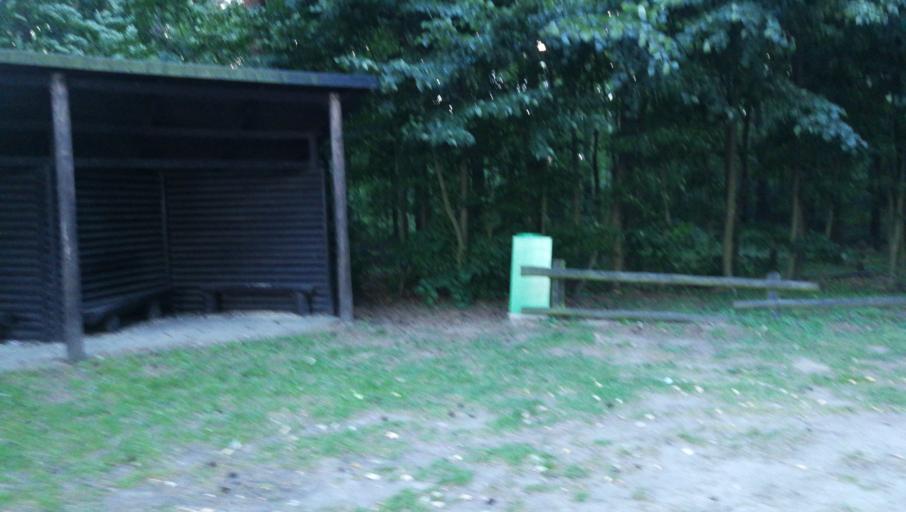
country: PL
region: Kujawsko-Pomorskie
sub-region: Powiat wloclawski
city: Boniewo
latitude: 52.4059
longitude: 18.8703
